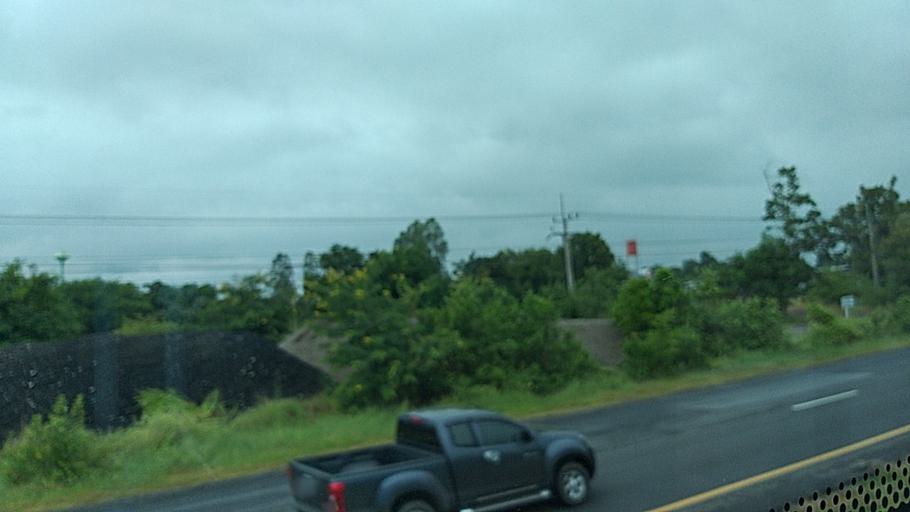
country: TH
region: Nakhon Ratchasima
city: Sida
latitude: 15.6043
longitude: 102.5620
